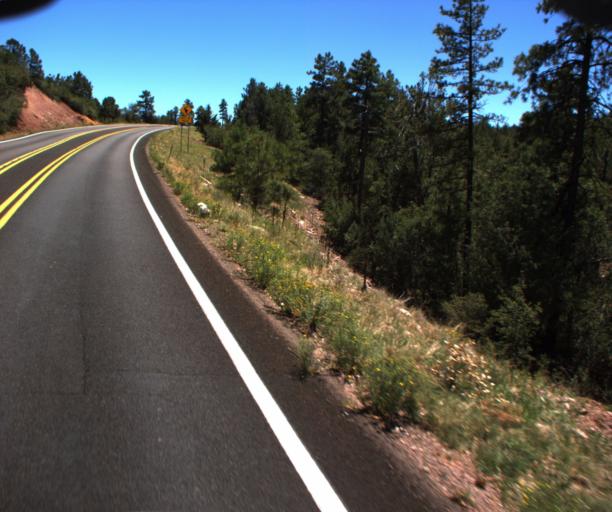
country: US
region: Arizona
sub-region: Gila County
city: Pine
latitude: 34.3620
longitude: -111.4261
